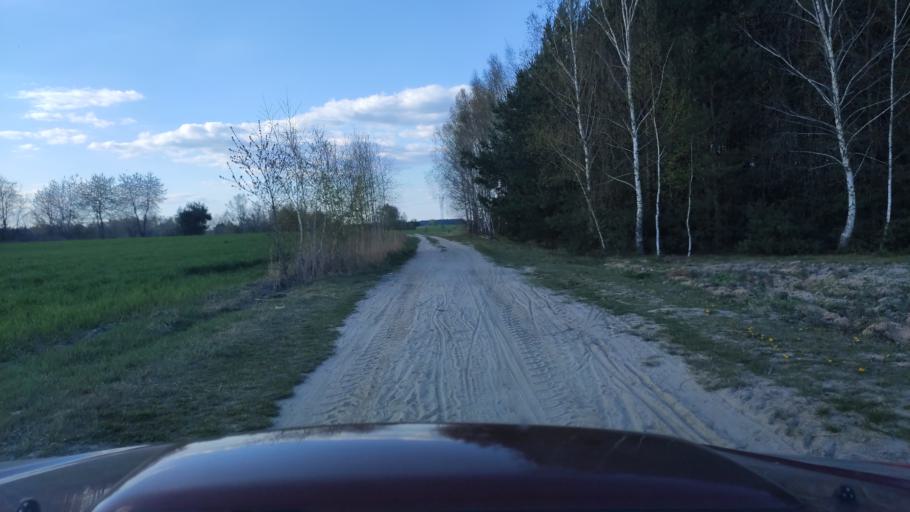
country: PL
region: Masovian Voivodeship
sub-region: Powiat zwolenski
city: Zwolen
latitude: 51.3682
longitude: 21.5749
